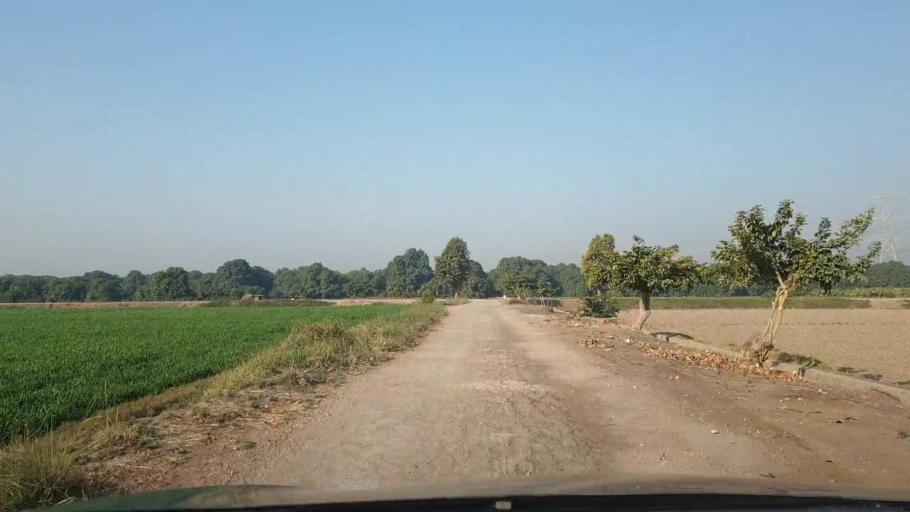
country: PK
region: Sindh
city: Tando Allahyar
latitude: 25.4933
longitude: 68.7101
